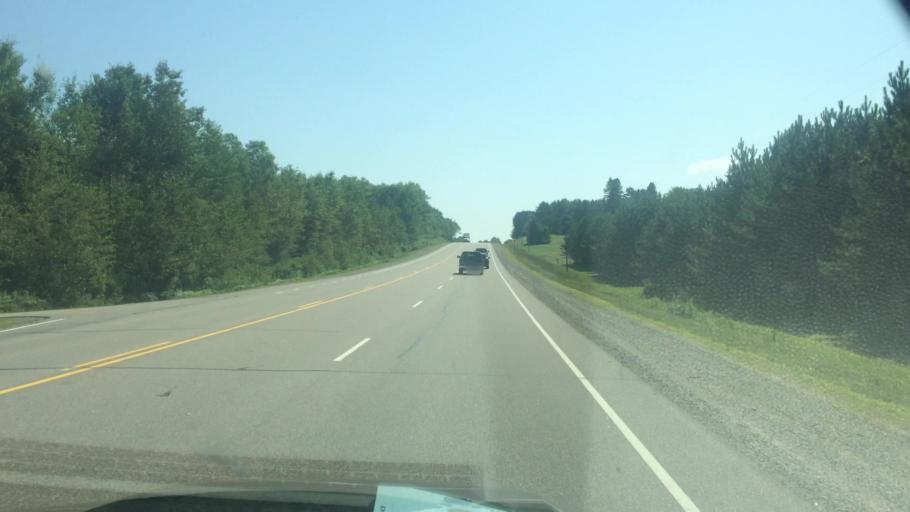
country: US
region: Wisconsin
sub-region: Lincoln County
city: Tomahawk
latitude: 45.5704
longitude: -89.5950
